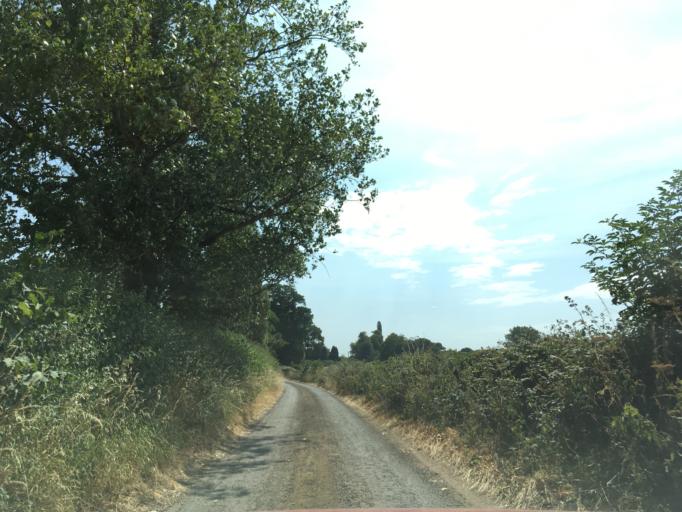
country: GB
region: England
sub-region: South Gloucestershire
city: Alveston
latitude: 51.5927
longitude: -2.5182
